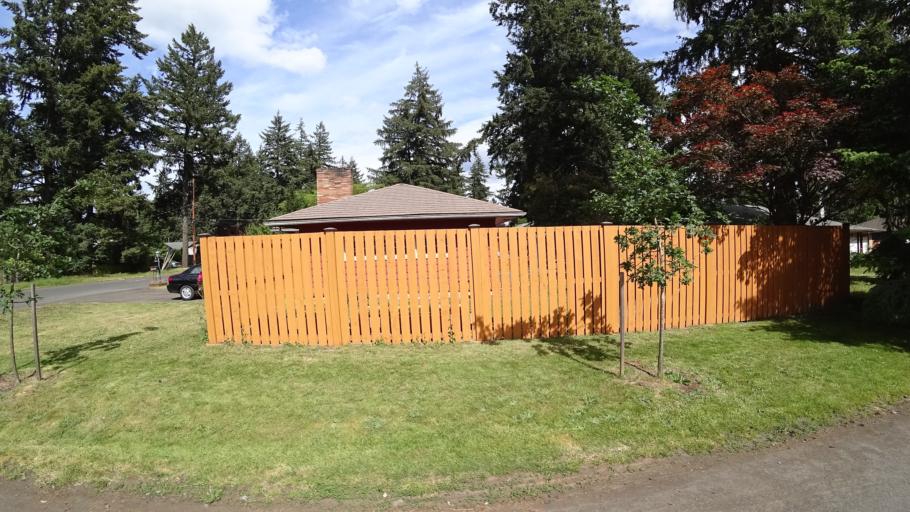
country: US
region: Oregon
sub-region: Multnomah County
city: Lents
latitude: 45.4943
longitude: -122.5435
